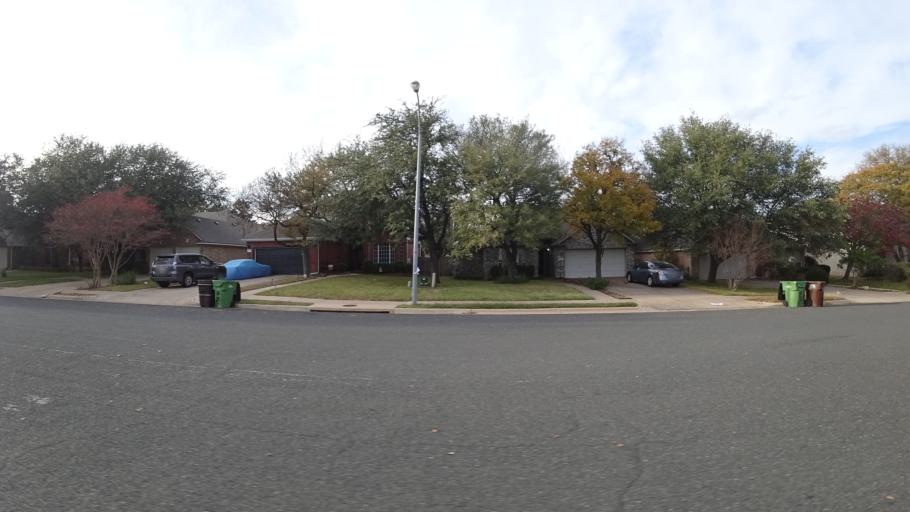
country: US
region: Texas
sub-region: Williamson County
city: Brushy Creek
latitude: 30.5177
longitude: -97.7244
